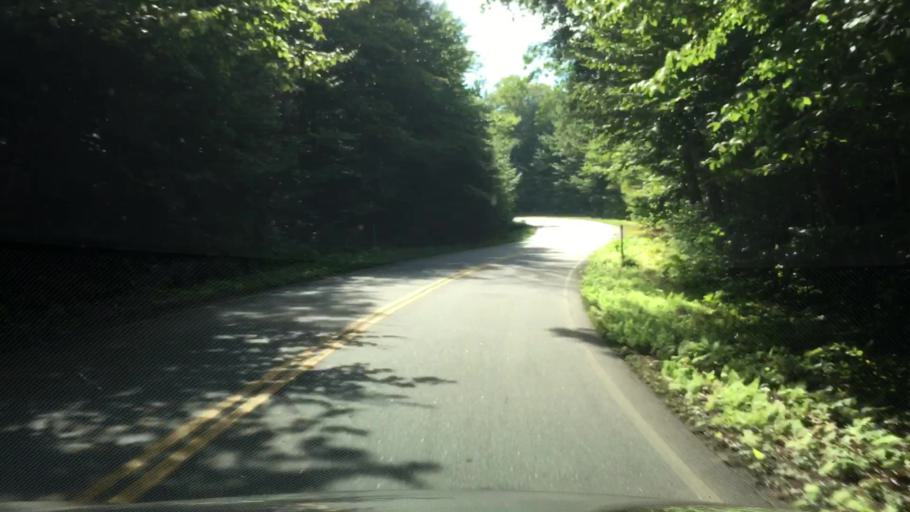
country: US
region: New Hampshire
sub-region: Carroll County
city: North Conway
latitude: 44.0516
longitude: -71.2739
